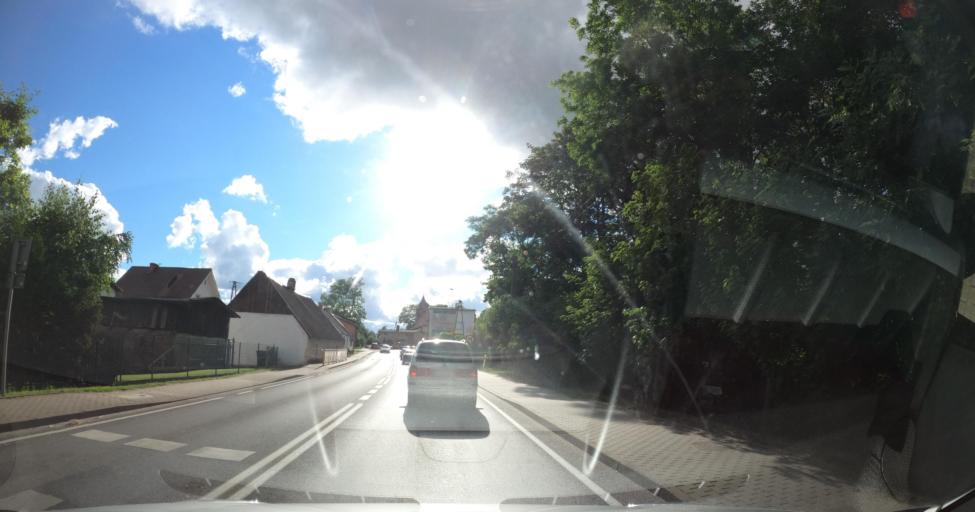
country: PL
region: Pomeranian Voivodeship
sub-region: Powiat kartuski
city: Zukowo
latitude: 54.3415
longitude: 18.3678
